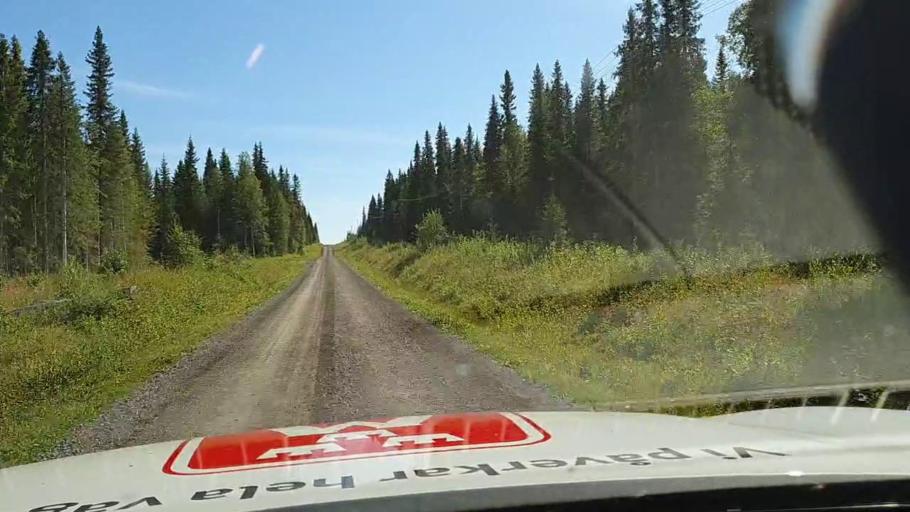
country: SE
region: Jaemtland
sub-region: Stroemsunds Kommun
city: Stroemsund
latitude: 63.7819
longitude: 15.3086
